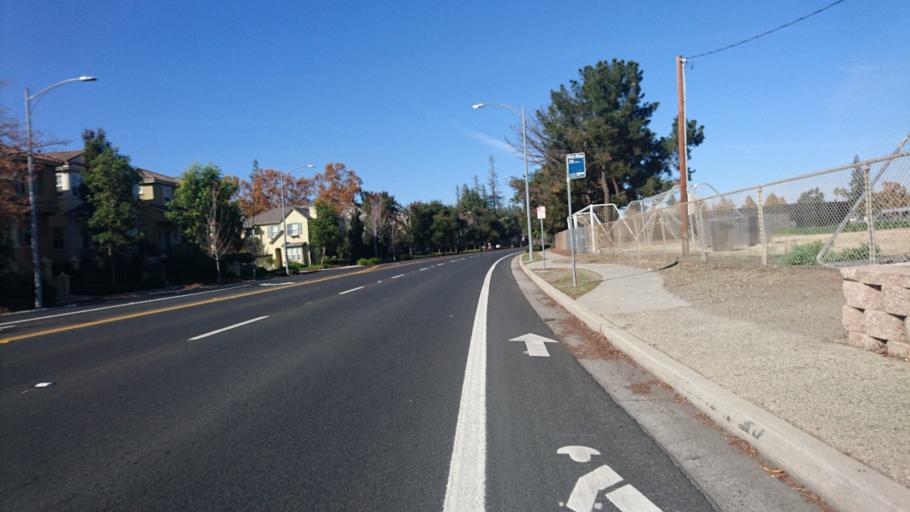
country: US
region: California
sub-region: Santa Clara County
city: Campbell
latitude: 37.2865
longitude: -121.9846
